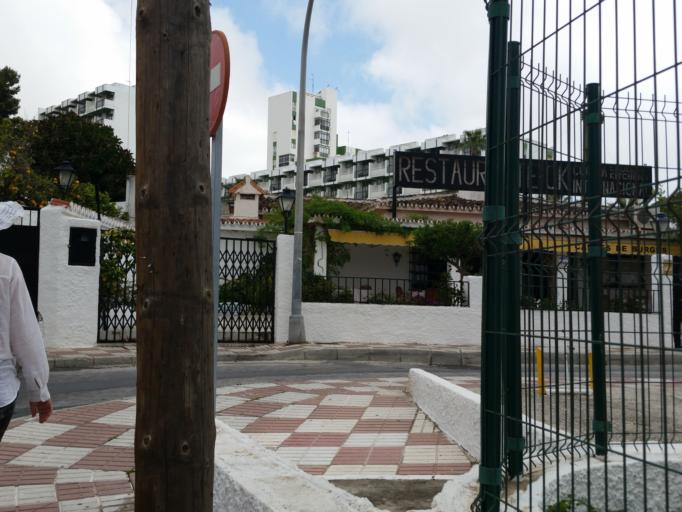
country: ES
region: Andalusia
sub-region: Provincia de Malaga
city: Torremolinos
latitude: 36.5946
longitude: -4.5245
